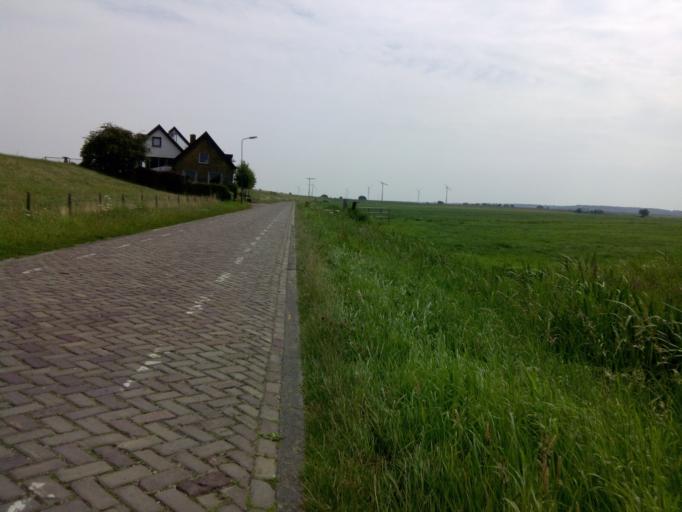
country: NL
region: Utrecht
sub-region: Gemeente Bunschoten
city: Spakenburg
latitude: 52.2676
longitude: 5.3460
